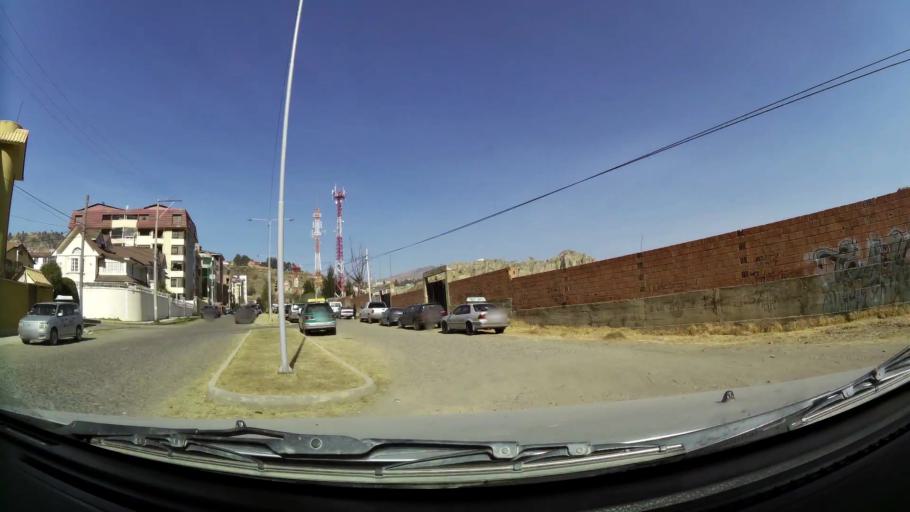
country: BO
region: La Paz
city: La Paz
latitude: -16.5144
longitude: -68.0637
